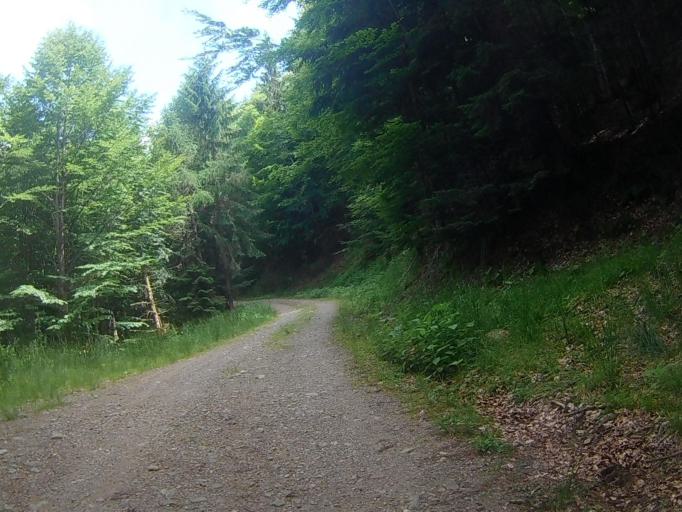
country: SI
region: Selnica ob Dravi
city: Selnica ob Dravi
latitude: 46.5075
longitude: 15.4836
